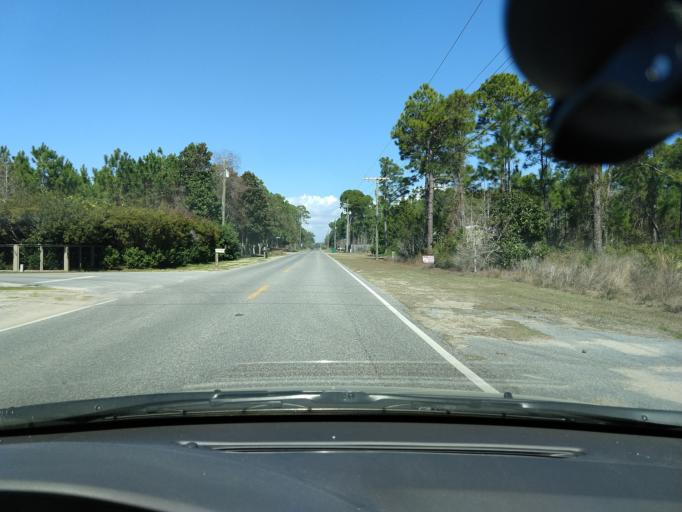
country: US
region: Florida
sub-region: Walton County
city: Miramar Beach
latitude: 30.3795
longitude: -86.2879
